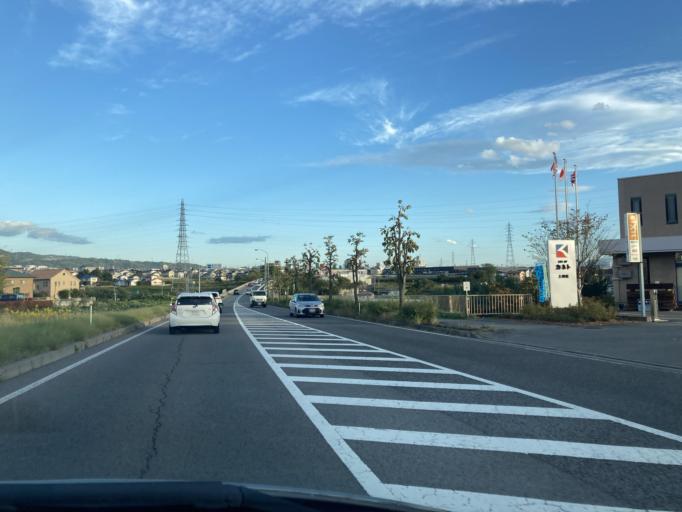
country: JP
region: Nagano
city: Ueda
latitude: 36.4092
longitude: 138.2670
